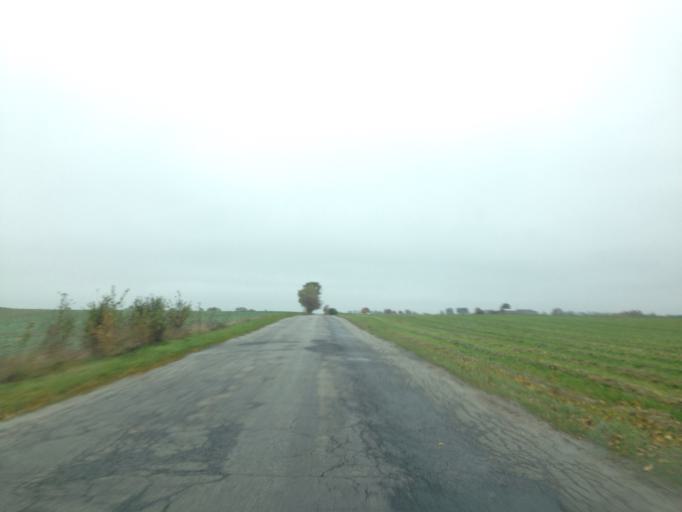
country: PL
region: Kujawsko-Pomorskie
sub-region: Powiat brodnicki
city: Bartniczka
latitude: 53.2098
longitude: 19.5818
